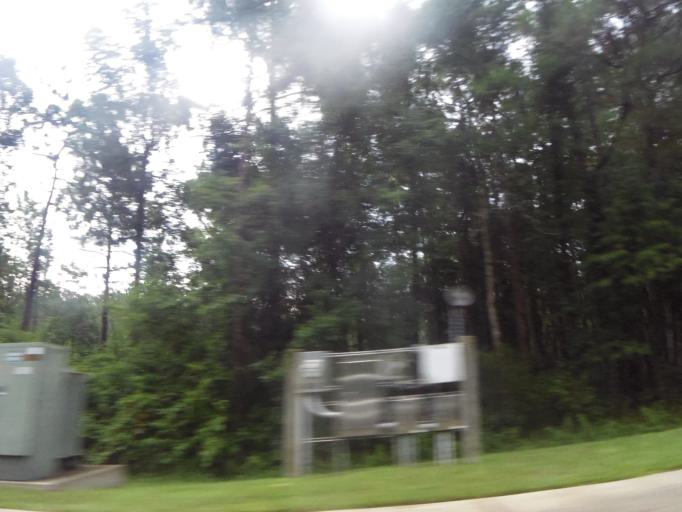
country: US
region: Florida
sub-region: Duval County
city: Jacksonville Beach
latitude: 30.2648
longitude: -81.5047
